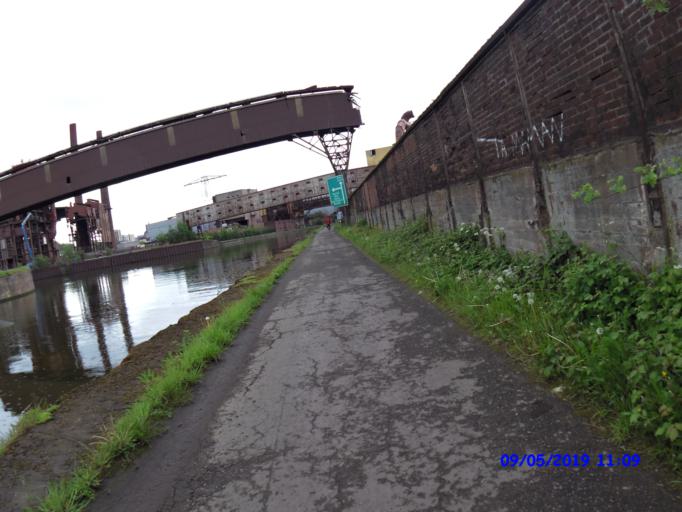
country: BE
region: Wallonia
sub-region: Province du Hainaut
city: Charleroi
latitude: 50.4111
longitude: 4.4228
